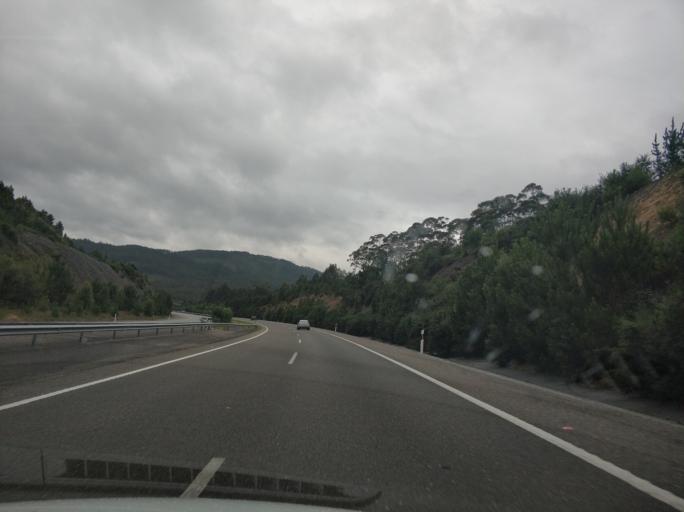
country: ES
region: Galicia
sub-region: Provincia de Lugo
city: Ribadeo
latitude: 43.5360
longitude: -7.0913
